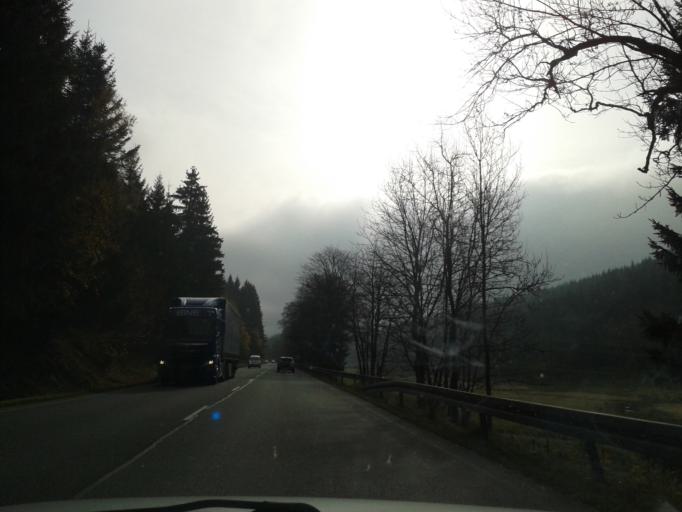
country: DE
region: North Rhine-Westphalia
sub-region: Regierungsbezirk Arnsberg
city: Winterberg
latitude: 51.2345
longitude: 8.5296
